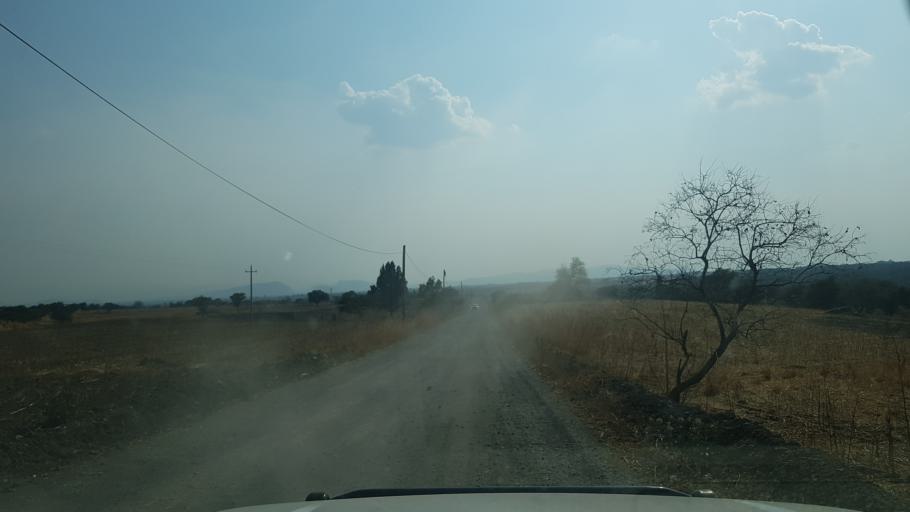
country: MX
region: Morelos
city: Tlacotepec
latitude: 18.7779
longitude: -98.7285
